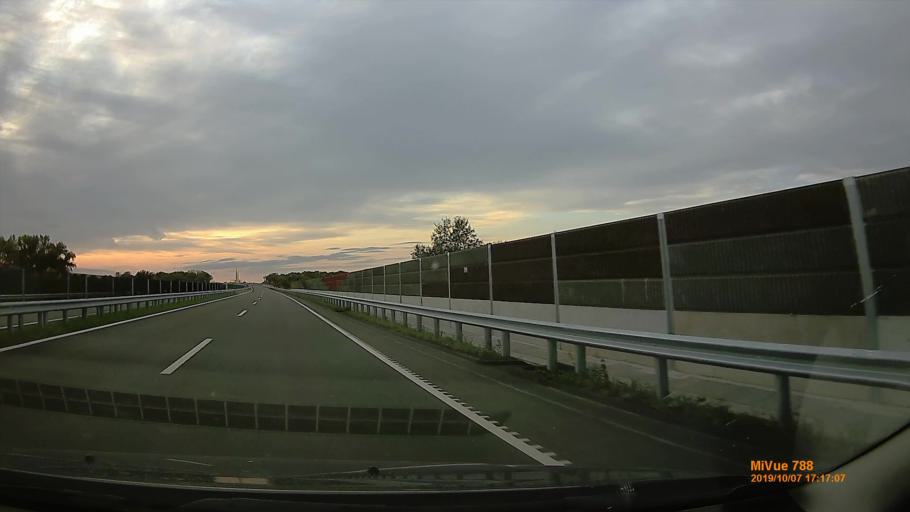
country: HU
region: Jasz-Nagykun-Szolnok
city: Kunszentmarton
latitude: 46.8628
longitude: 20.2954
